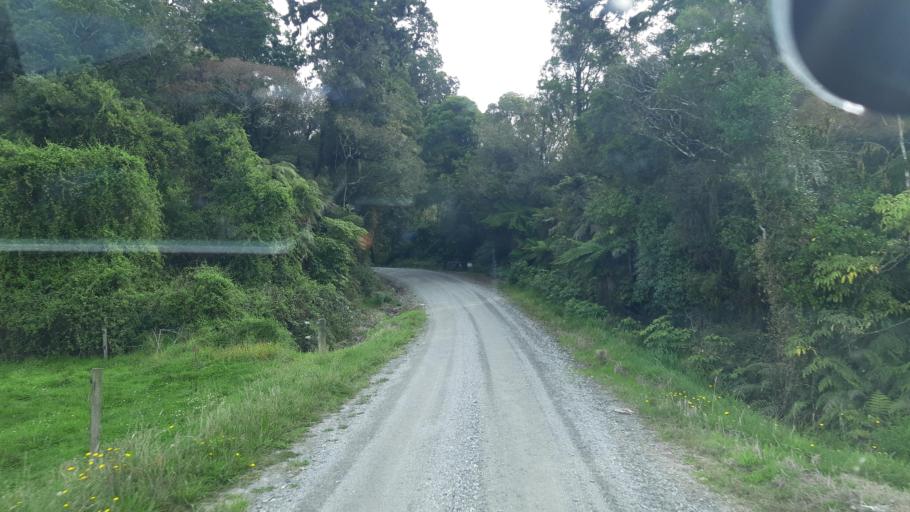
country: NZ
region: West Coast
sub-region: Westland District
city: Hokitika
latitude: -43.1116
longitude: 170.4730
